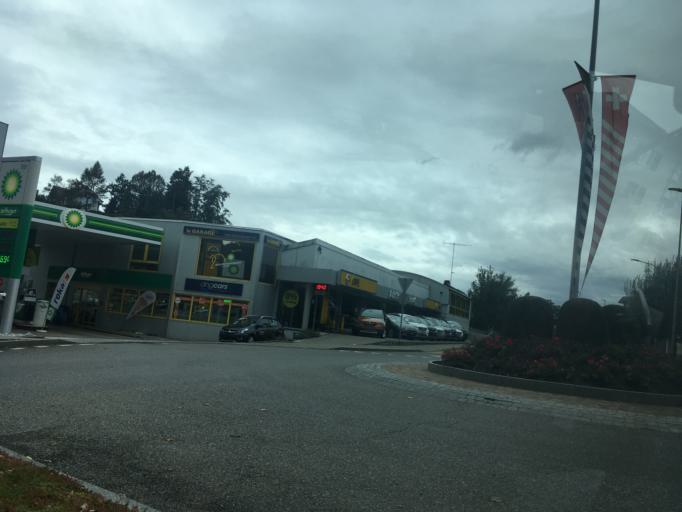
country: CH
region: Fribourg
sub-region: Sense District
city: Tafers
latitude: 46.8151
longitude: 7.2159
